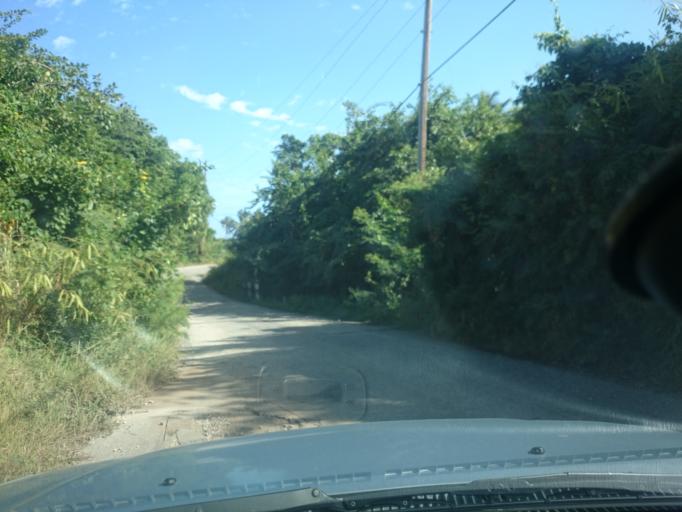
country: BB
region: Saint Lucy
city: Checker Hall
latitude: 13.3262
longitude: -59.6056
